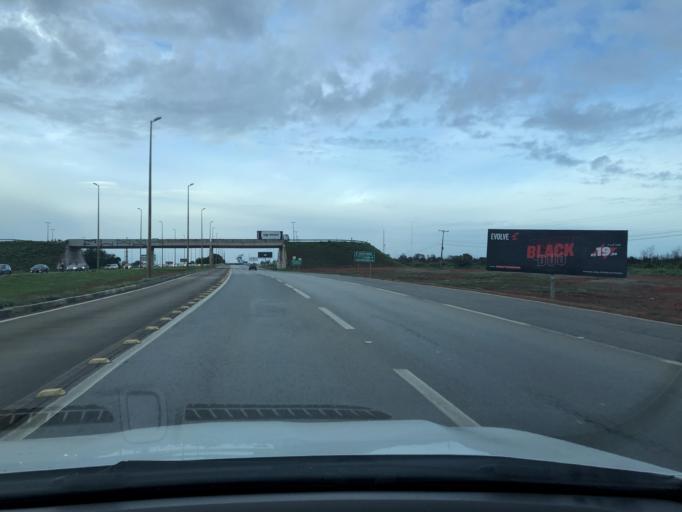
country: BR
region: Federal District
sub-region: Brasilia
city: Brasilia
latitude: -15.9715
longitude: -47.9910
